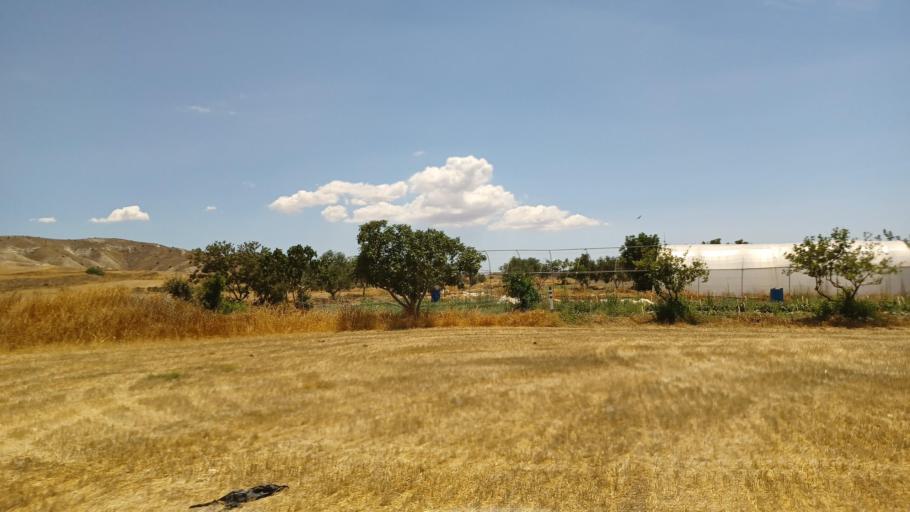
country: CY
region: Larnaka
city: Troulloi
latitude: 35.0348
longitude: 33.6267
